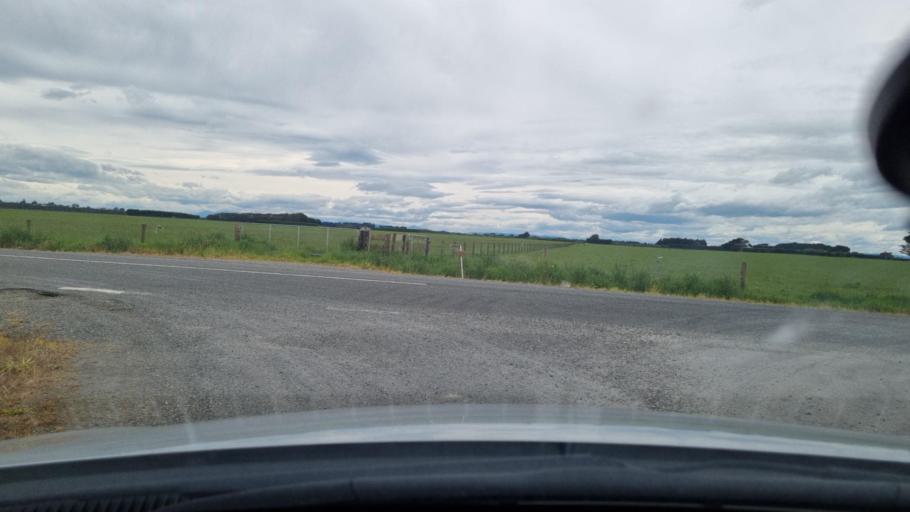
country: NZ
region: Southland
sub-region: Invercargill City
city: Invercargill
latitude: -46.3694
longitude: 168.2985
